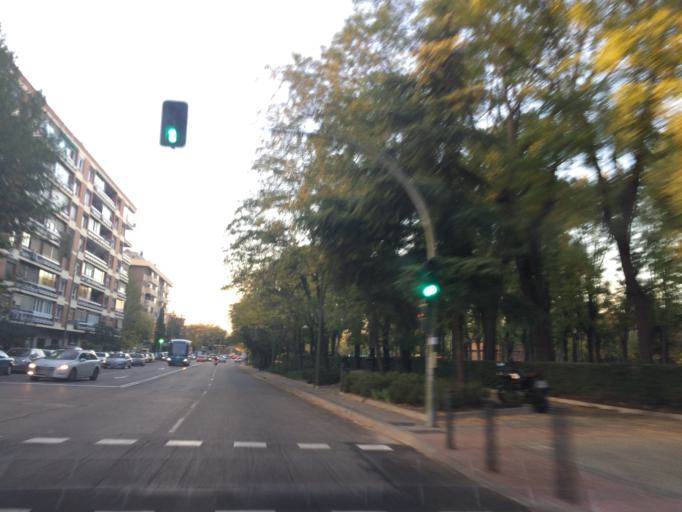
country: ES
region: Madrid
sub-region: Provincia de Madrid
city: Moncloa-Aravaca
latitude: 40.4315
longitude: -3.7319
